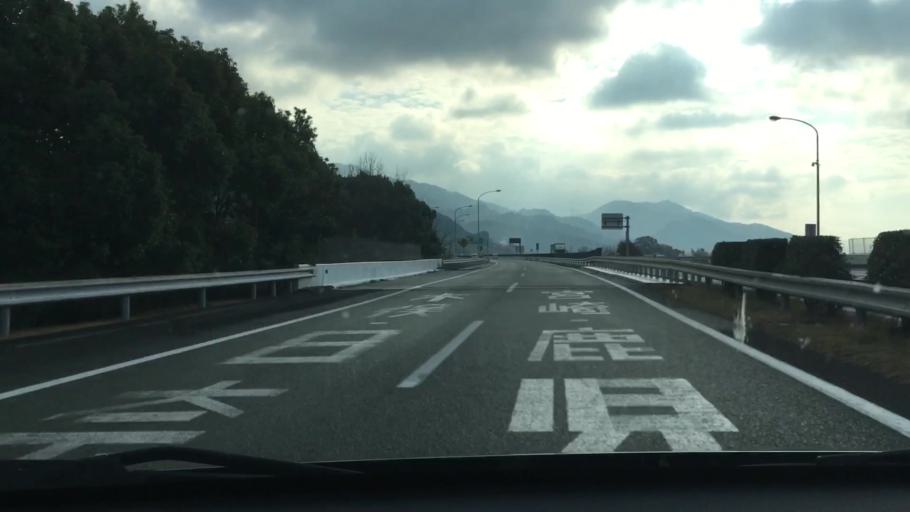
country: JP
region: Kumamoto
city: Yatsushiro
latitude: 32.5131
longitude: 130.6480
